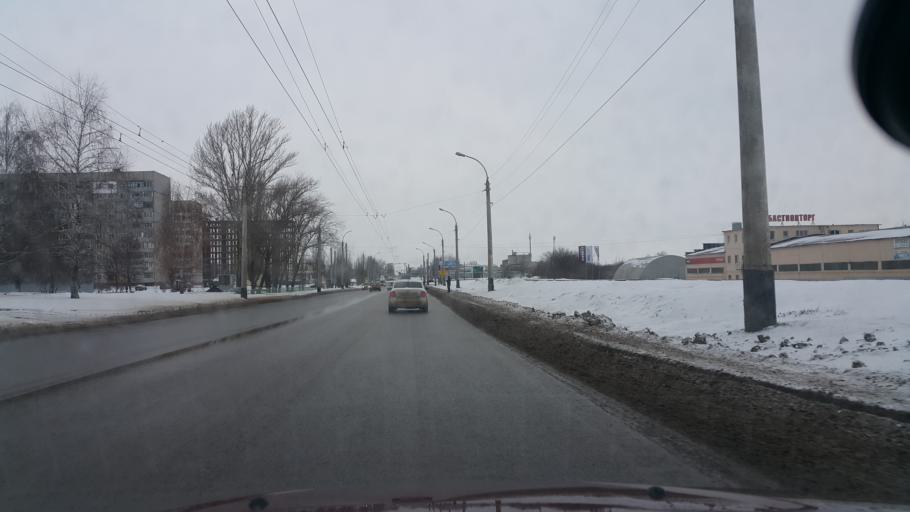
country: RU
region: Tambov
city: Tambov
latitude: 52.7374
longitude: 41.3823
